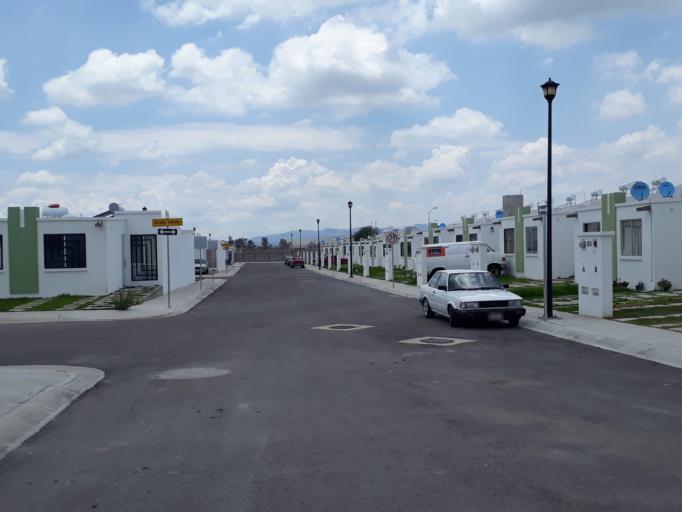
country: MX
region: Aguascalientes
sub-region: Aguascalientes
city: San Sebastian [Fraccionamiento]
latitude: 21.8058
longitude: -102.2726
